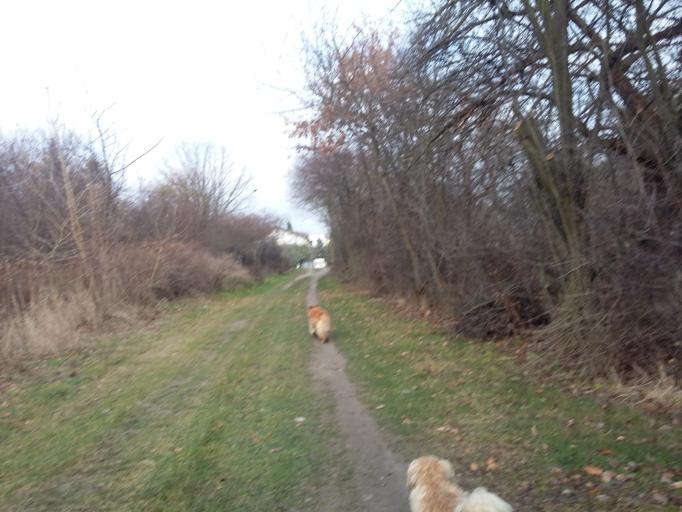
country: PL
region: Lodz Voivodeship
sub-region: Powiat pabianicki
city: Ksawerow
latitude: 51.7373
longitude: 19.4119
